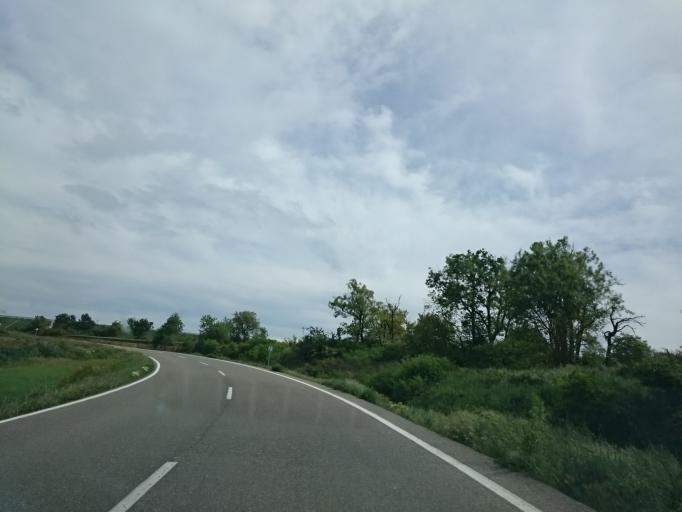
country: ES
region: Catalonia
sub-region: Provincia de Lleida
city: Ivorra
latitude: 41.7337
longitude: 1.3834
